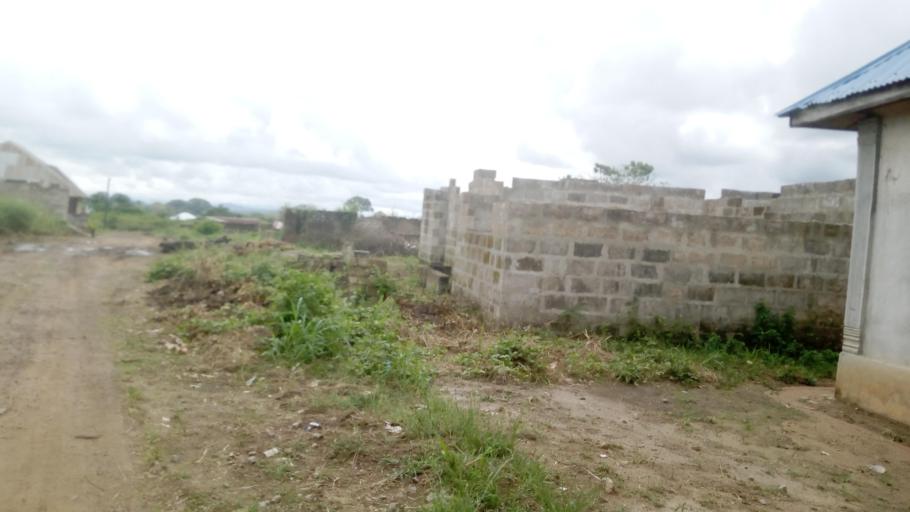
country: SL
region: Northern Province
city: Makeni
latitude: 8.9005
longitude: -12.0240
